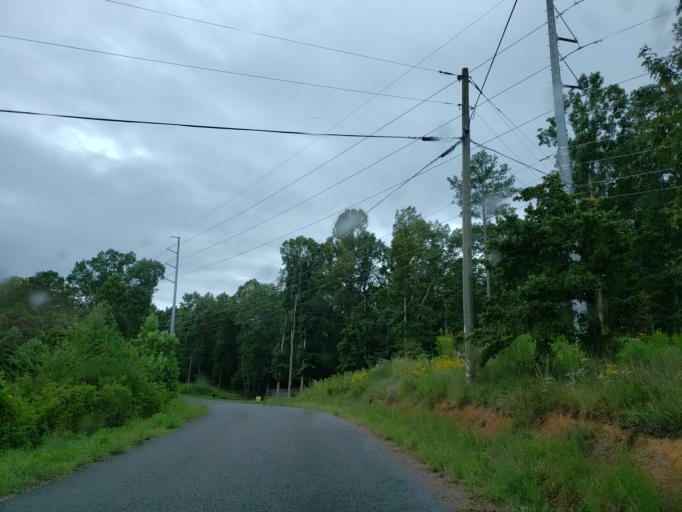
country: US
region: Georgia
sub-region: Gilmer County
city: Ellijay
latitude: 34.6209
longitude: -84.5780
